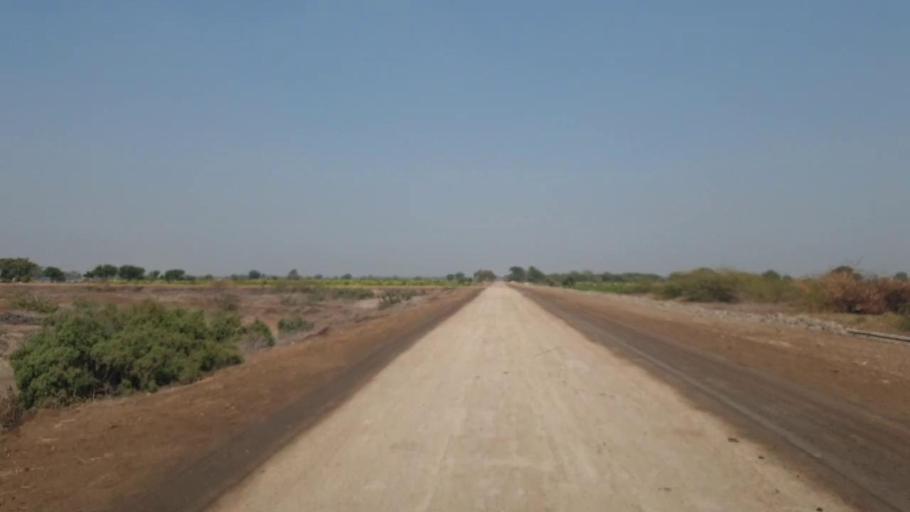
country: PK
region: Sindh
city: Mirwah Gorchani
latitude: 25.3696
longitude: 68.9316
